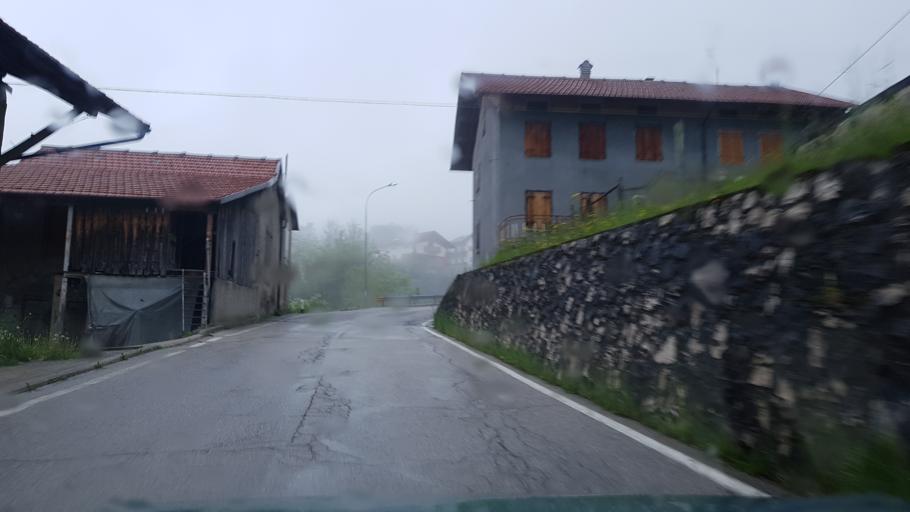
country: IT
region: Veneto
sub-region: Provincia di Belluno
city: Lamosano
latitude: 46.1650
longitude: 12.3900
